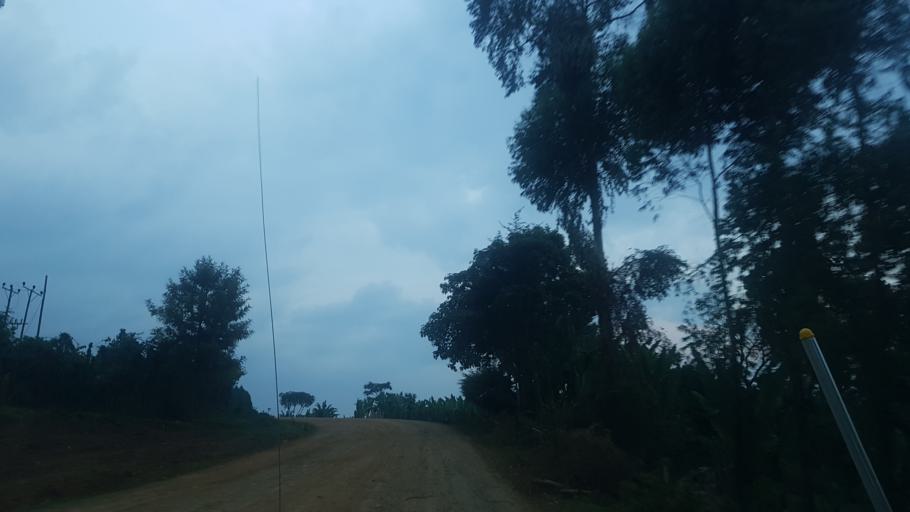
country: ET
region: Oromiya
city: Gore
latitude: 7.7848
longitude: 35.4599
